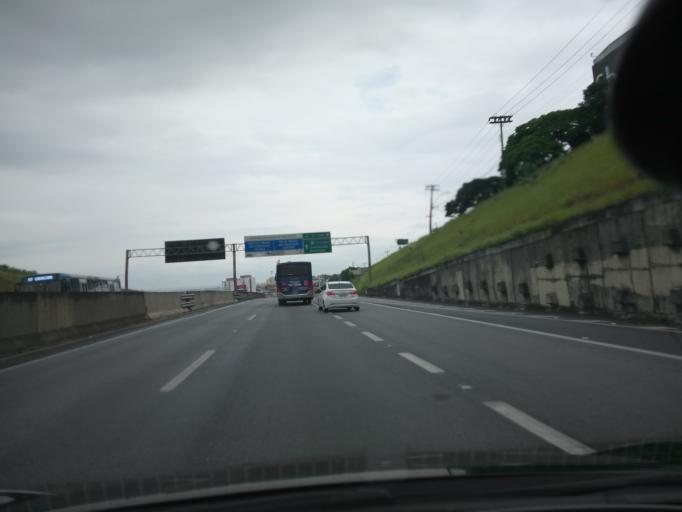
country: BR
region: Sao Paulo
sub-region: Campinas
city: Campinas
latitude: -22.9337
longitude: -47.0775
